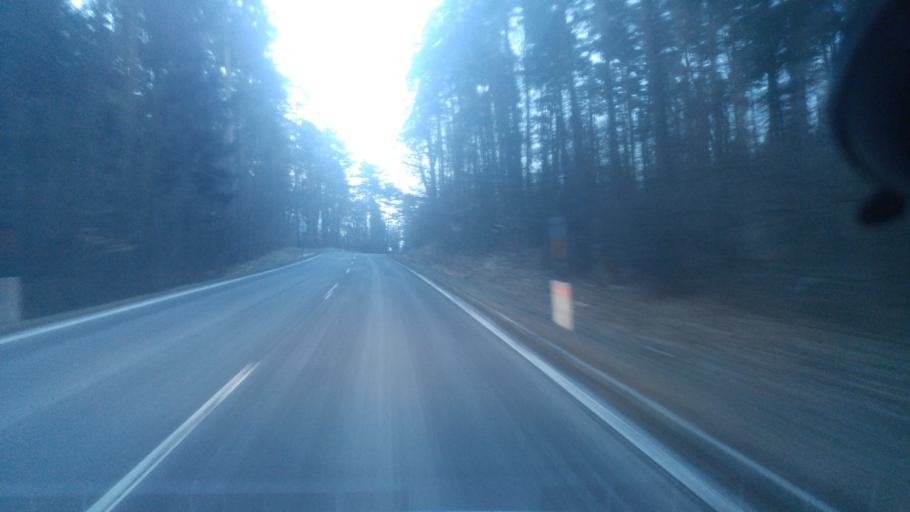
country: AT
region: Lower Austria
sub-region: Politischer Bezirk Baden
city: Berndorf
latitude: 47.9554
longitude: 16.1343
